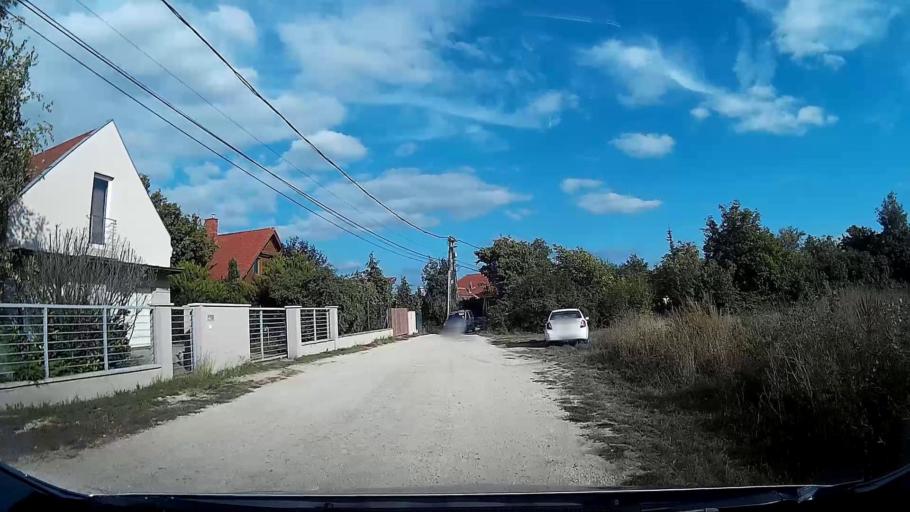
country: HU
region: Pest
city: Nagykovacsi
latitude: 47.6412
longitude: 19.0179
